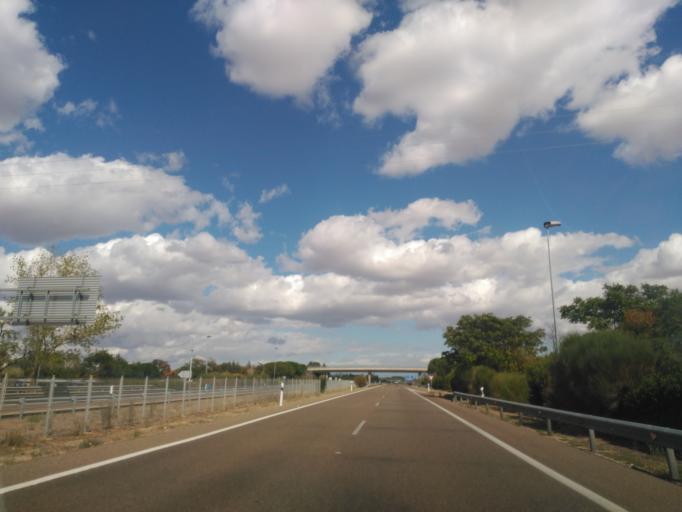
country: ES
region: Castille and Leon
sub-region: Provincia de Palencia
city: Torquemada
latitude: 42.0312
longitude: -4.2997
